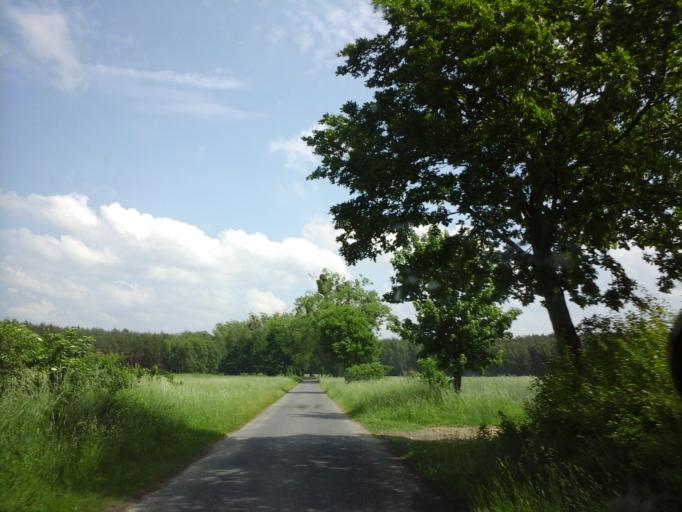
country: PL
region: West Pomeranian Voivodeship
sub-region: Powiat choszczenski
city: Drawno
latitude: 53.1897
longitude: 15.8323
